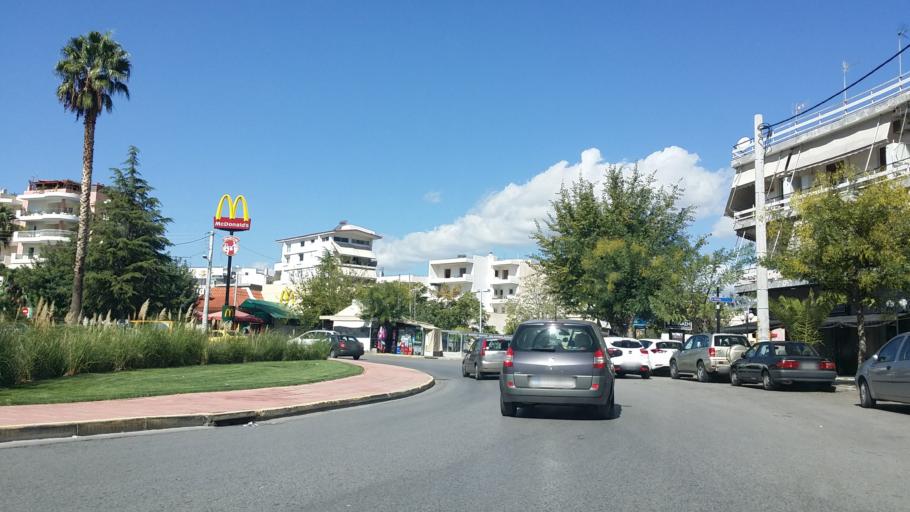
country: GR
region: Attica
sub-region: Nomarchia Athinas
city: Agioi Anargyroi
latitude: 38.0309
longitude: 23.7132
